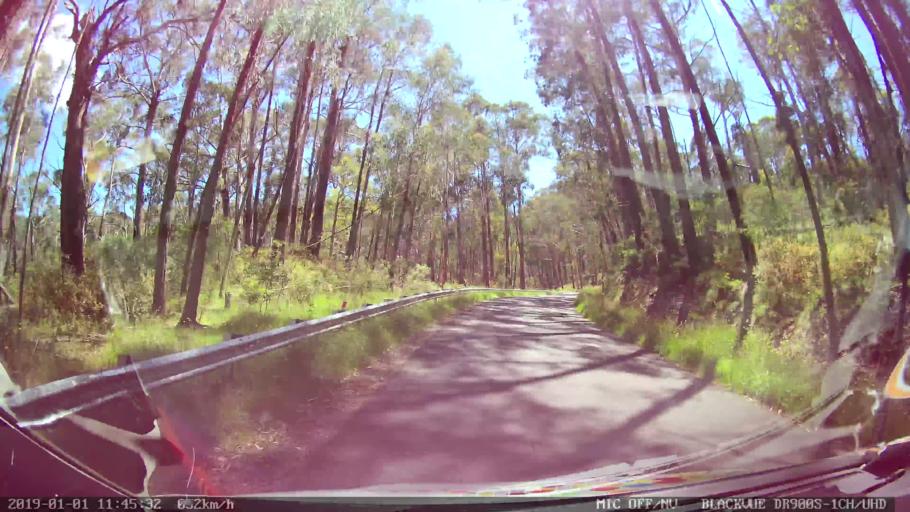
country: AU
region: New South Wales
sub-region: Snowy River
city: Jindabyne
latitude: -35.8959
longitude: 148.3960
